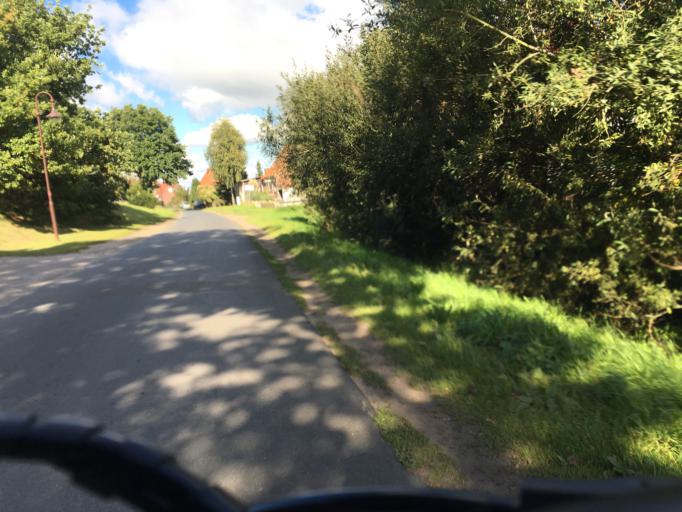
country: DE
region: Lower Saxony
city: Bardowick
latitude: 53.3088
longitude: 10.3808
